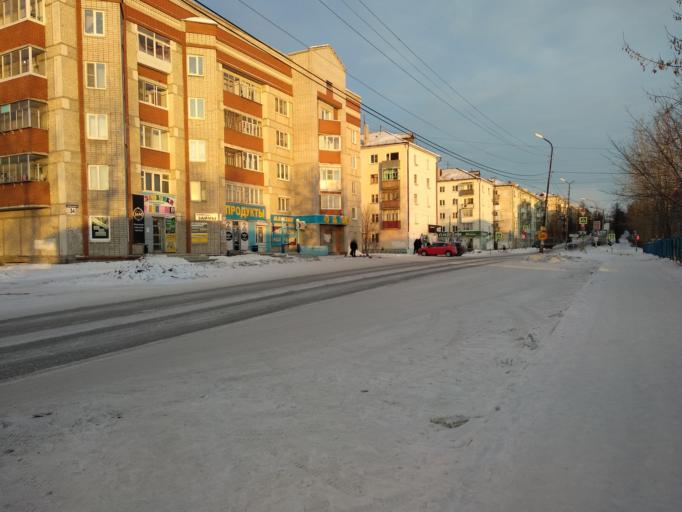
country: RU
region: Sverdlovsk
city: Krasnotur'insk
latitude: 59.7621
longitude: 60.2058
